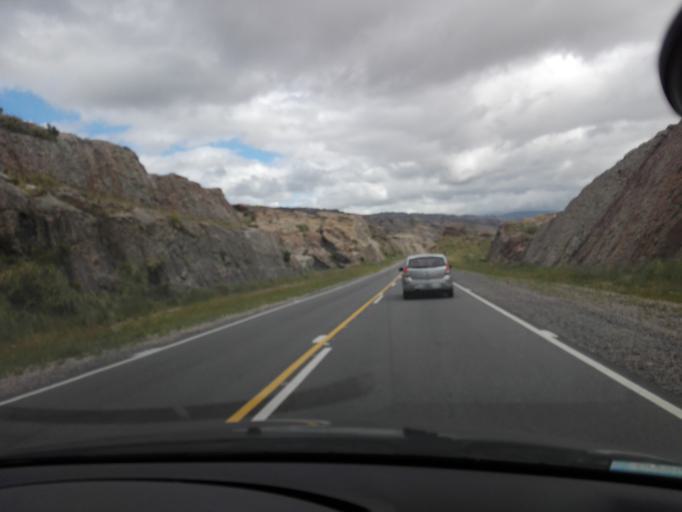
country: AR
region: Cordoba
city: Mina Clavero
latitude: -31.6414
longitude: -64.9055
